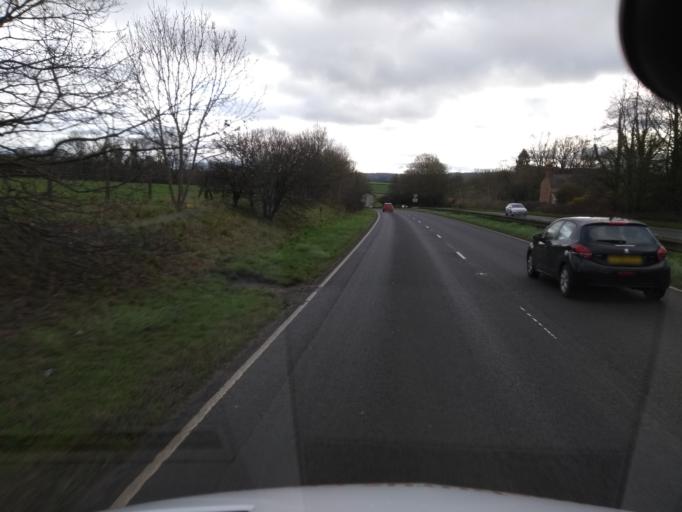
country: GB
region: England
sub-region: Dorset
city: Sherborne
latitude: 50.9451
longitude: -2.5705
